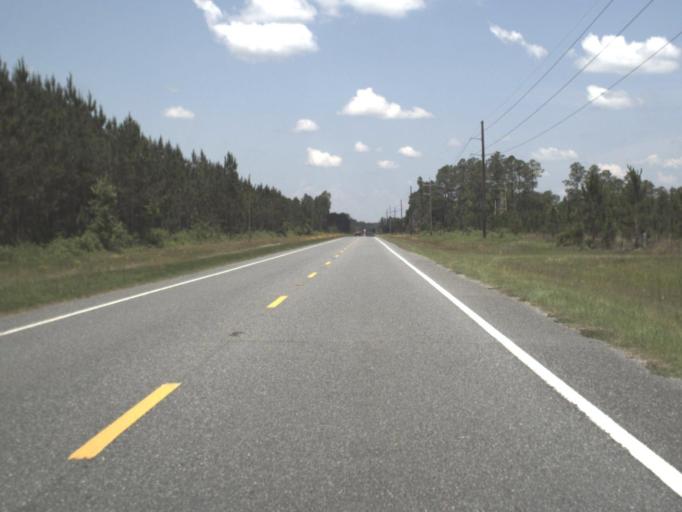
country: US
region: Florida
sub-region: Union County
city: Lake Butler
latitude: 29.9784
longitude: -82.2311
